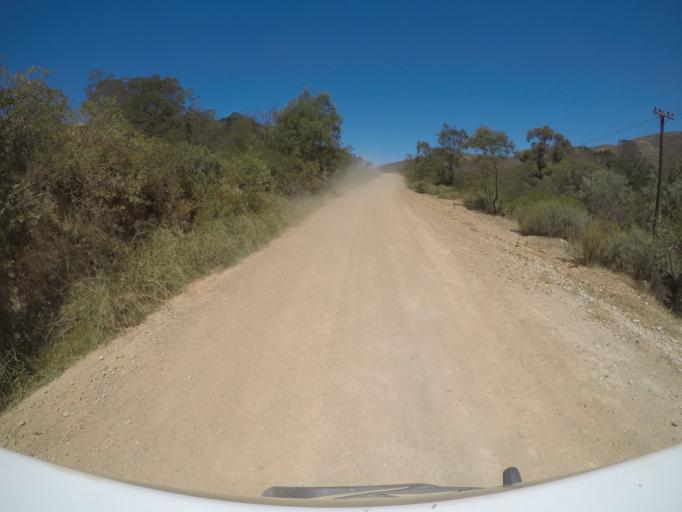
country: ZA
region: Western Cape
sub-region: Overberg District Municipality
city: Caledon
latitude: -34.1246
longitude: 19.2393
